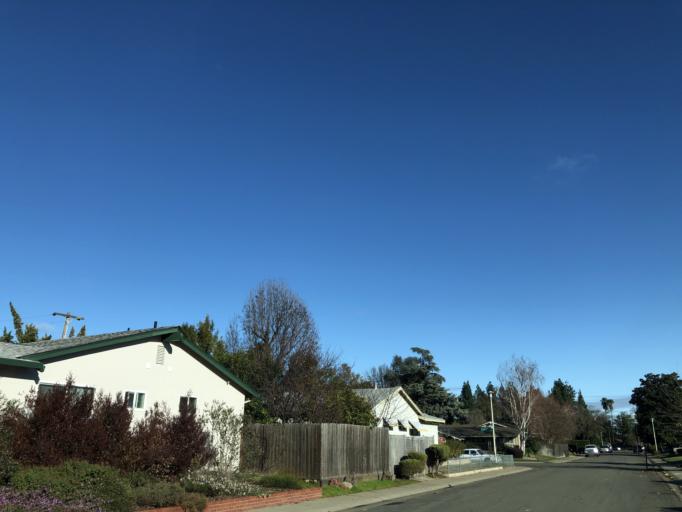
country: US
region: California
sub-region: Sacramento County
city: Rosemont
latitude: 38.5528
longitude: -121.4032
